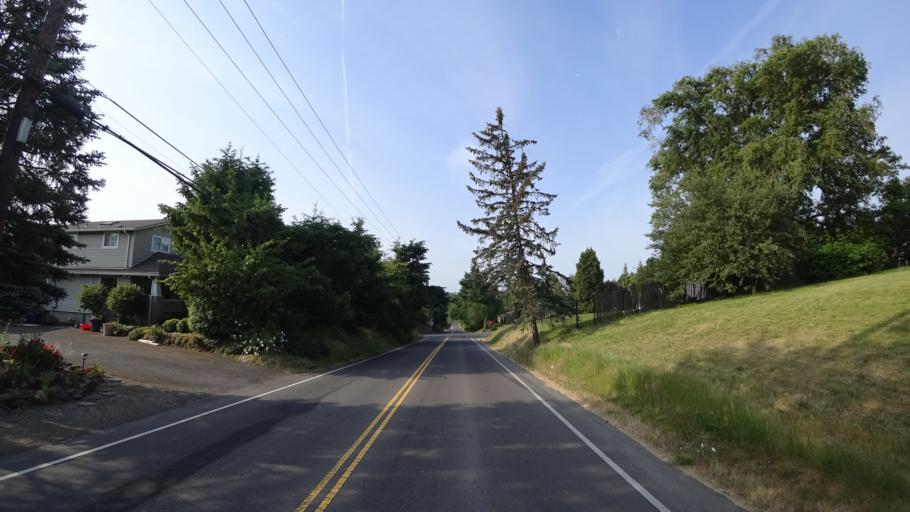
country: US
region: Oregon
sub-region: Clackamas County
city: Happy Valley
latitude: 45.4548
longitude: -122.5276
